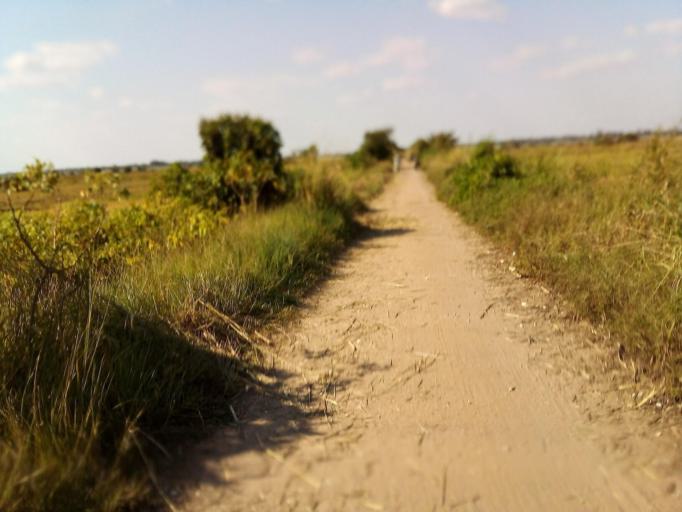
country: MZ
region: Zambezia
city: Quelimane
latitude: -17.5898
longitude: 36.8362
